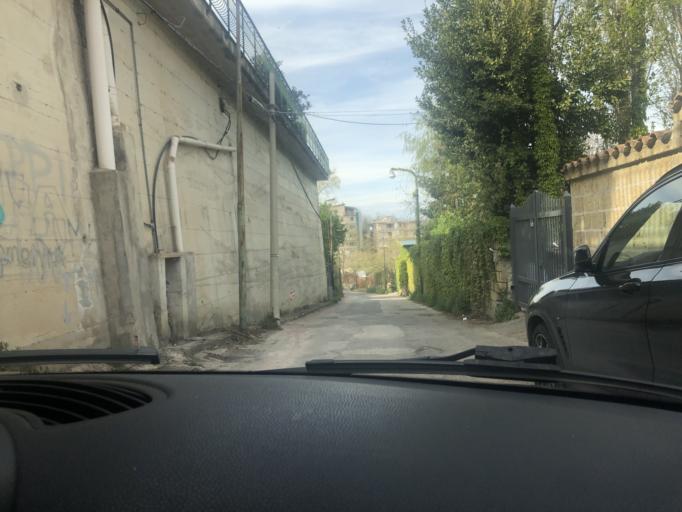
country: IT
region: Campania
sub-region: Provincia di Napoli
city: Torre Caracciolo
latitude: 40.8697
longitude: 14.1932
